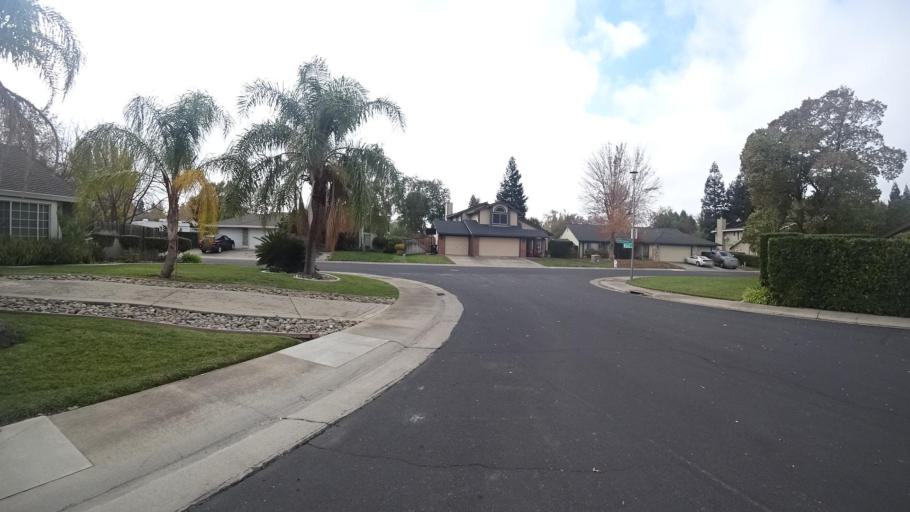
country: US
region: California
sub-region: Sacramento County
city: Elk Grove
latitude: 38.4192
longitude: -121.3595
